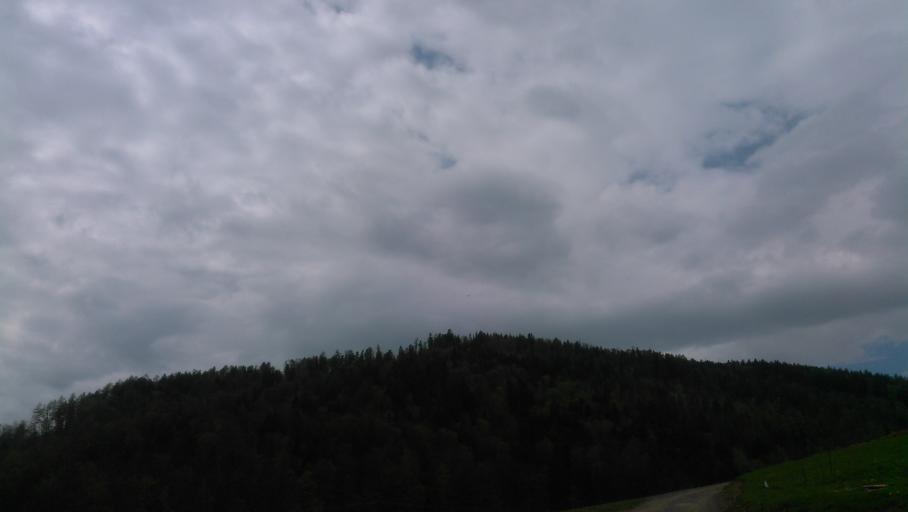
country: SK
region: Banskobystricky
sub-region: Okres Banska Bystrica
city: Brezno
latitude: 48.8462
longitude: 19.6104
